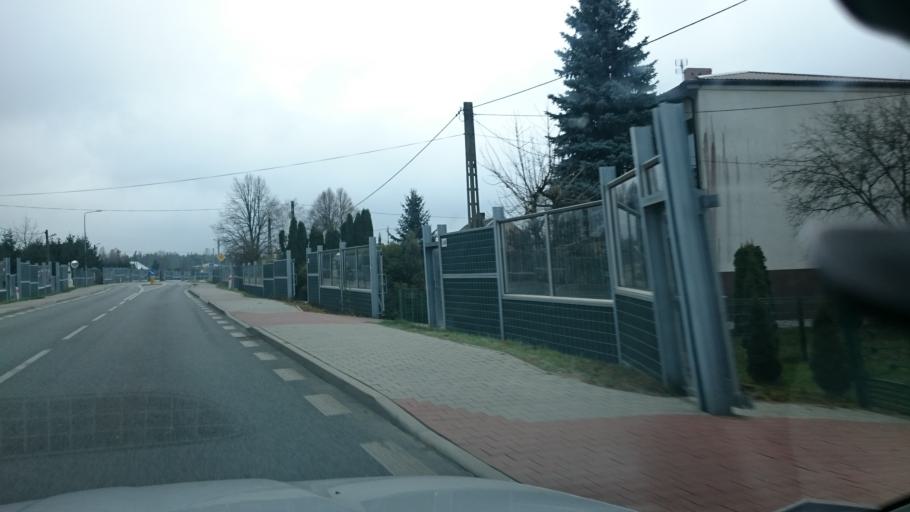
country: PL
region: Swietokrzyskie
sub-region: Powiat konecki
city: Konskie
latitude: 51.1431
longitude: 20.3639
